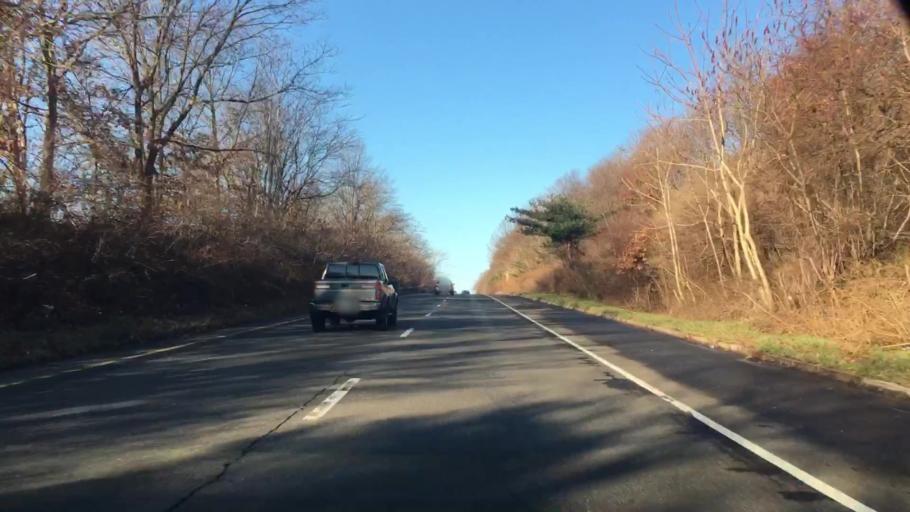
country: US
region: New York
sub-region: Suffolk County
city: Melville
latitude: 40.7835
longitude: -73.4356
